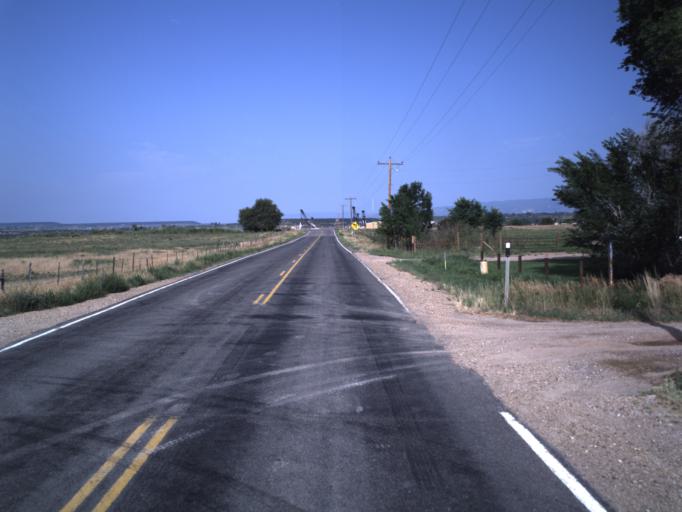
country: US
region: Utah
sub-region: Duchesne County
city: Duchesne
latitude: 40.3592
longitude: -110.3034
